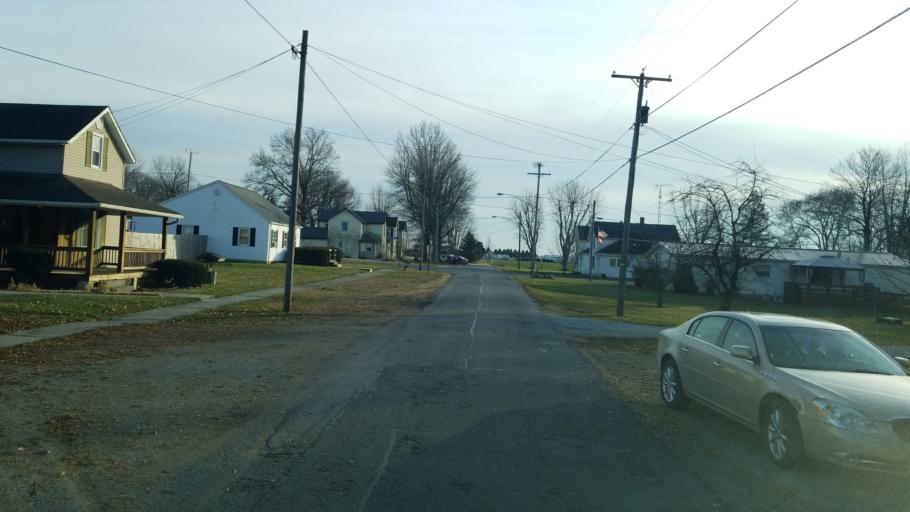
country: US
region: Ohio
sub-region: Marion County
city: Marion
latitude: 40.6839
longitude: -83.2136
